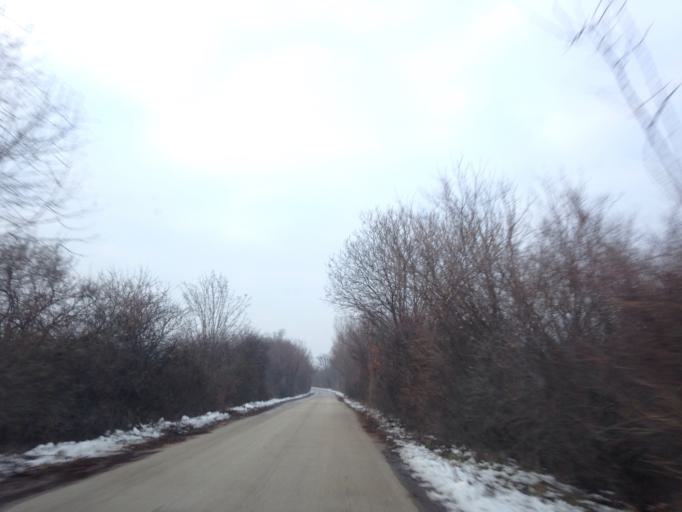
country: SK
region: Nitriansky
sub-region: Okres Nitra
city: Vrable
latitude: 48.0911
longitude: 18.3683
